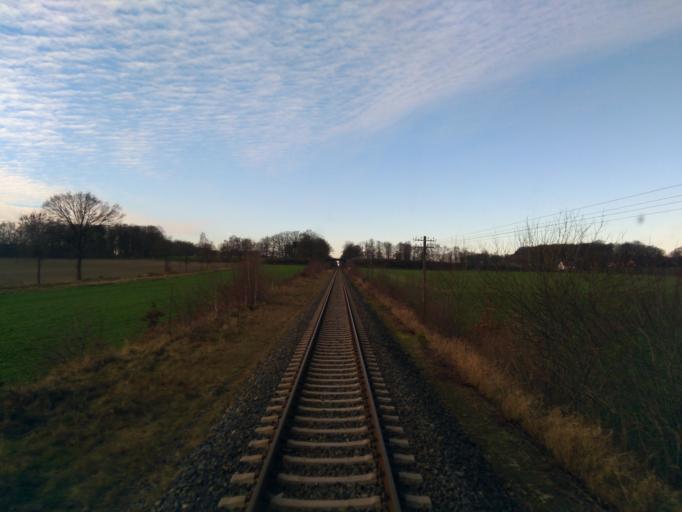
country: DE
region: Lower Saxony
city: Wriedel
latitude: 53.0058
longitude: 10.2978
